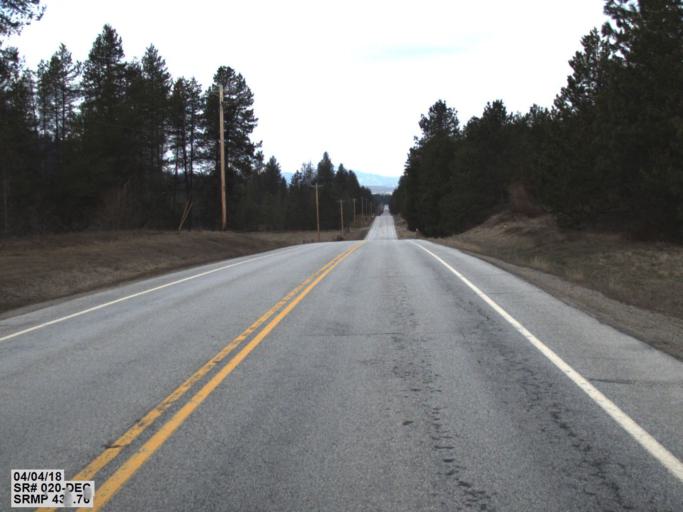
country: US
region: Washington
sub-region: Pend Oreille County
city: Newport
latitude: 48.2243
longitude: -117.1250
